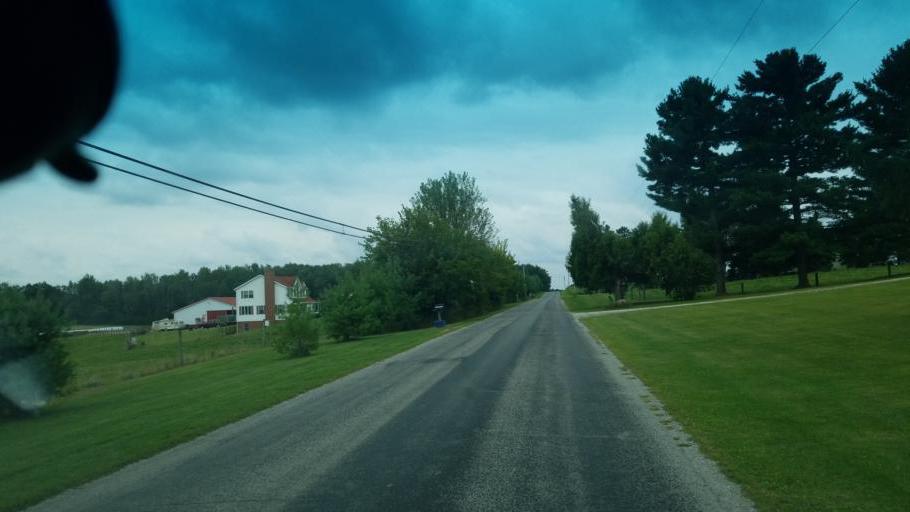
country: US
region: Ohio
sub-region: Huron County
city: Plymouth
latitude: 40.9521
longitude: -82.6005
